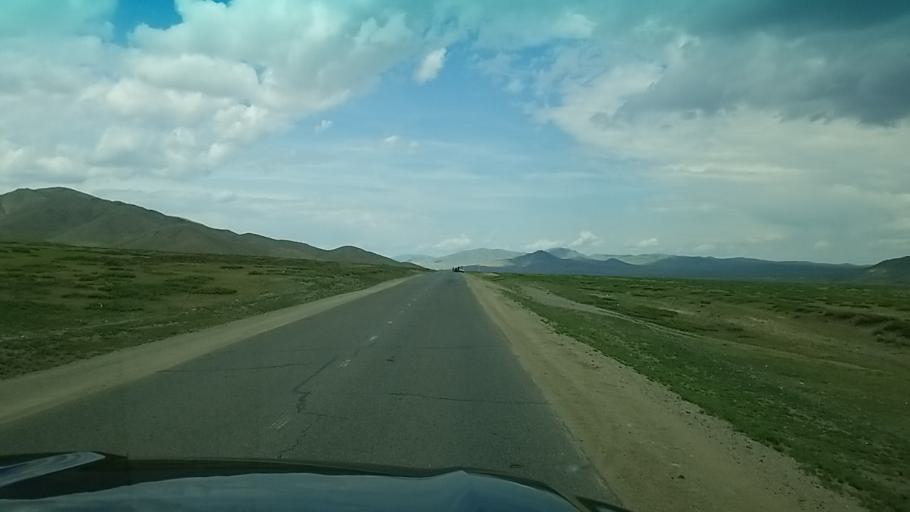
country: MN
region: Darhan Uul
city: Orhon
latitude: 49.7203
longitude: 106.1102
